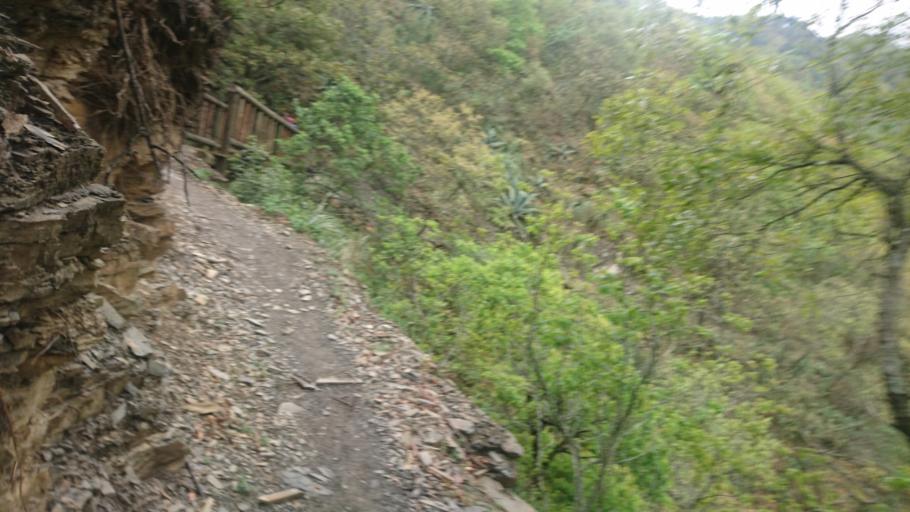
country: MX
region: Nuevo Leon
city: Garza Garcia
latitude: 25.6014
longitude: -100.3371
